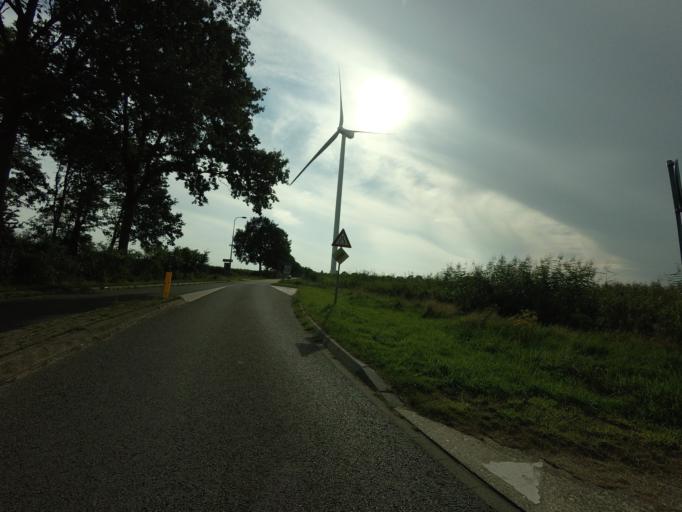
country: NL
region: Drenthe
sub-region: Gemeente Coevorden
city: Coevorden
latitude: 52.6428
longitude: 6.7152
